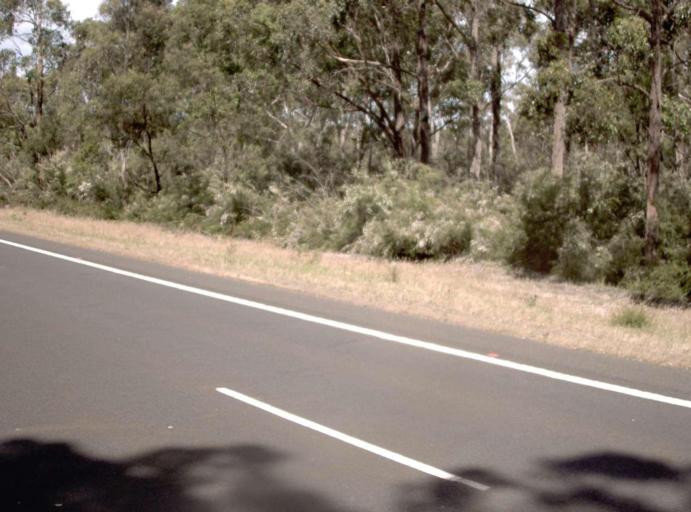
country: AU
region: Victoria
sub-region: East Gippsland
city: Bairnsdale
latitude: -37.9103
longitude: 147.3148
